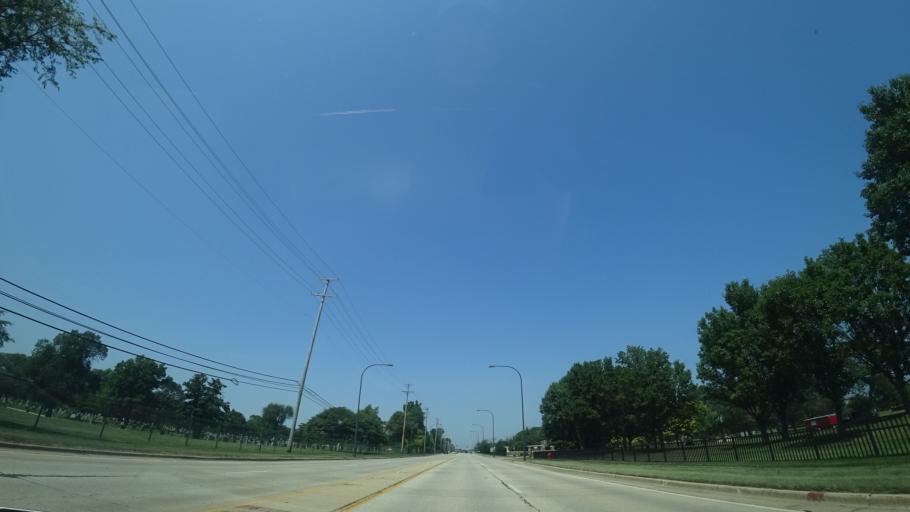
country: US
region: Illinois
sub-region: Cook County
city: Oak Lawn
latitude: 41.6866
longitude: -87.7590
